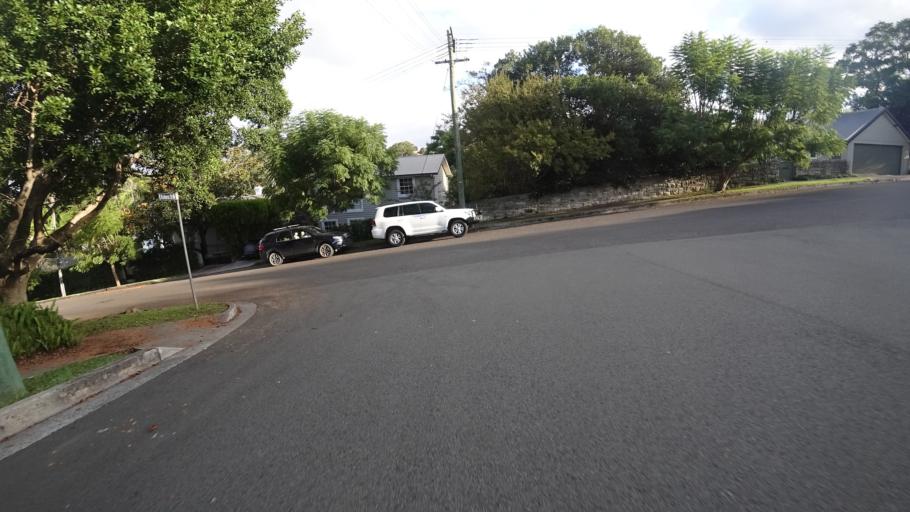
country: AU
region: New South Wales
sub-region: Lane Cove
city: Longueville
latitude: -33.8354
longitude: 151.1592
